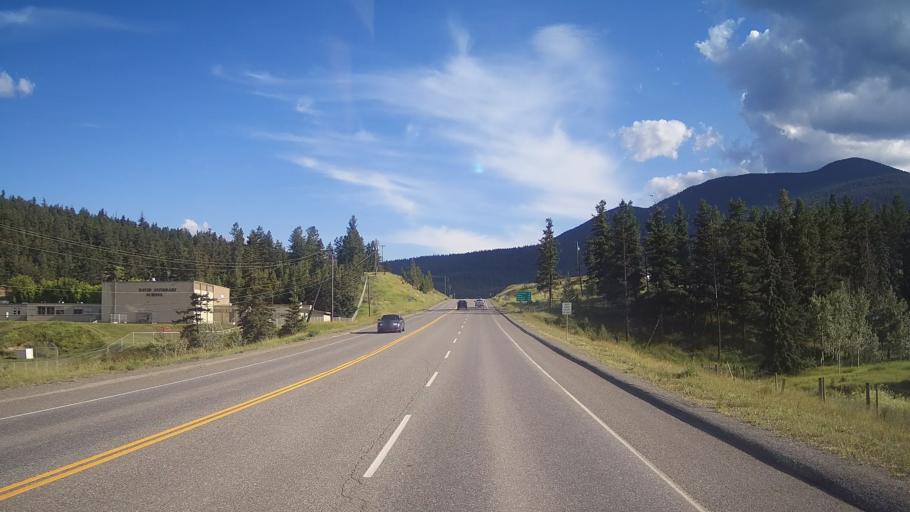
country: CA
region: British Columbia
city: Cache Creek
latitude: 51.0874
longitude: -121.5915
